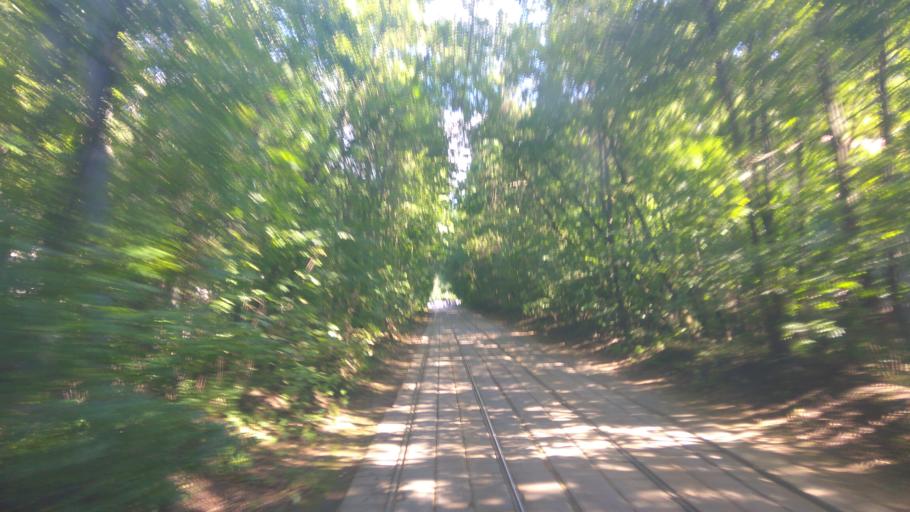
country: RU
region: Moscow
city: Sokol'niki
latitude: 55.8071
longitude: 37.6900
